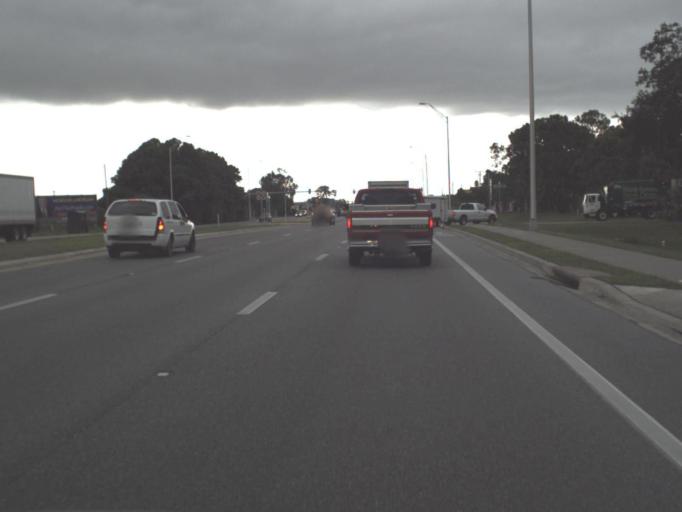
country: US
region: Florida
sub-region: Sarasota County
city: North Sarasota
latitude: 27.3771
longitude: -82.5310
